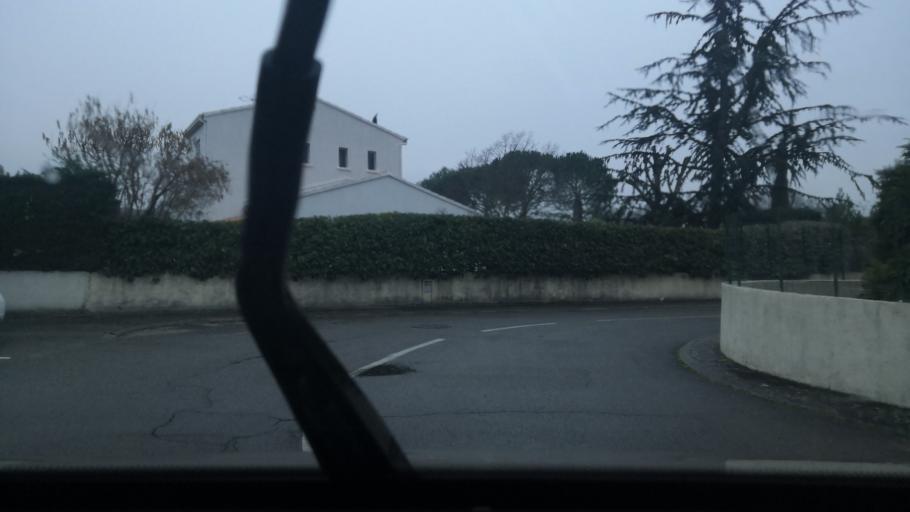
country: FR
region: Rhone-Alpes
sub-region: Departement de la Drome
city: Montelimar
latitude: 44.5490
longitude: 4.7709
